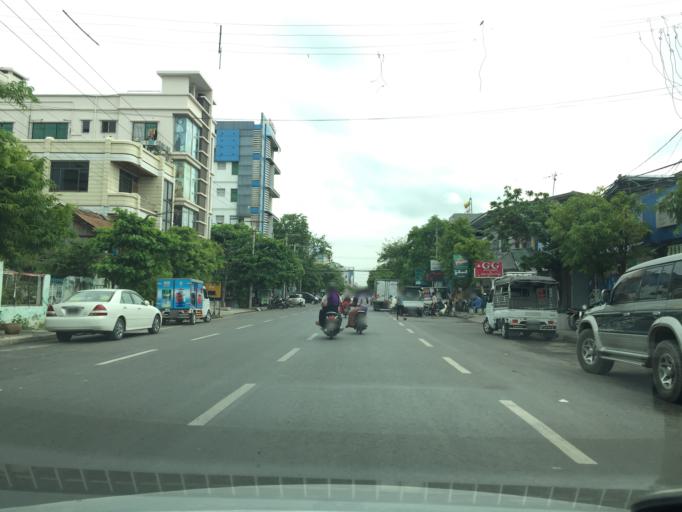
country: MM
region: Mandalay
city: Mandalay
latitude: 21.9734
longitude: 96.0789
